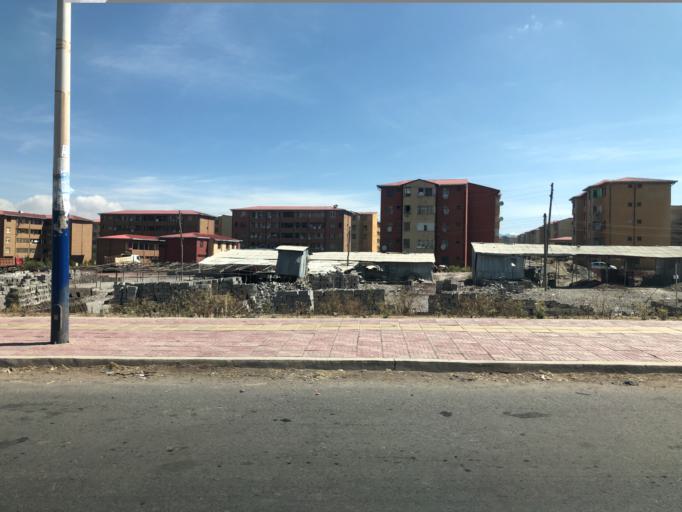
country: ET
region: Adis Abeba
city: Addis Ababa
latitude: 8.8751
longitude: 38.8198
